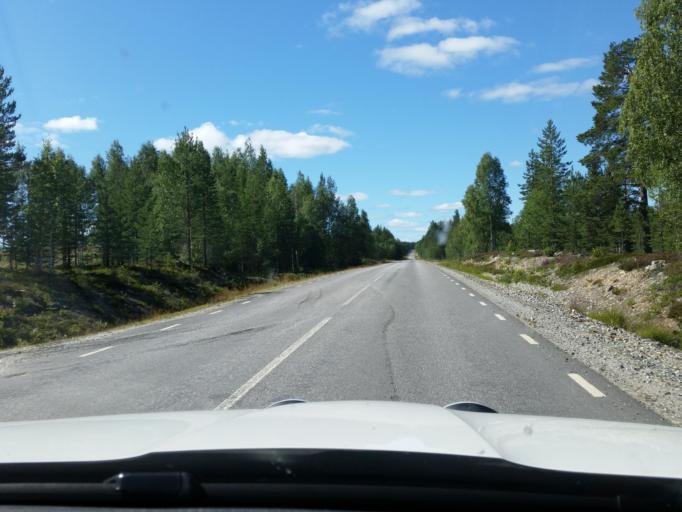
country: SE
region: Norrbotten
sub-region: Pitea Kommun
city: Roknas
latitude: 65.2094
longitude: 21.2142
